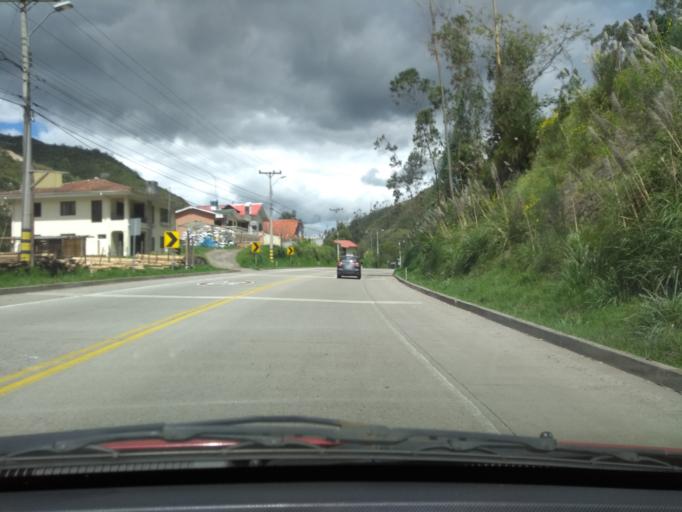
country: EC
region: Azuay
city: Cuenca
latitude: -2.9634
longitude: -79.0497
